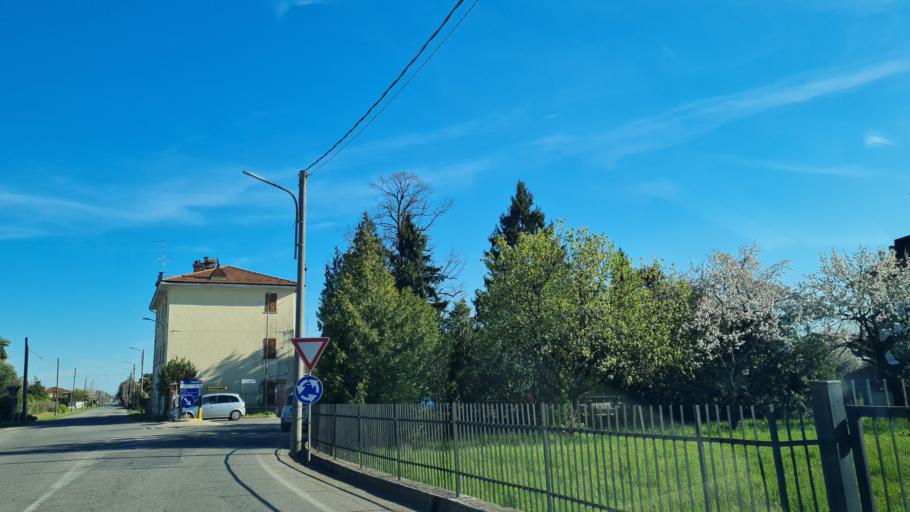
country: IT
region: Piedmont
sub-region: Provincia di Novara
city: Maggiora
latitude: 45.6881
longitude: 8.4272
